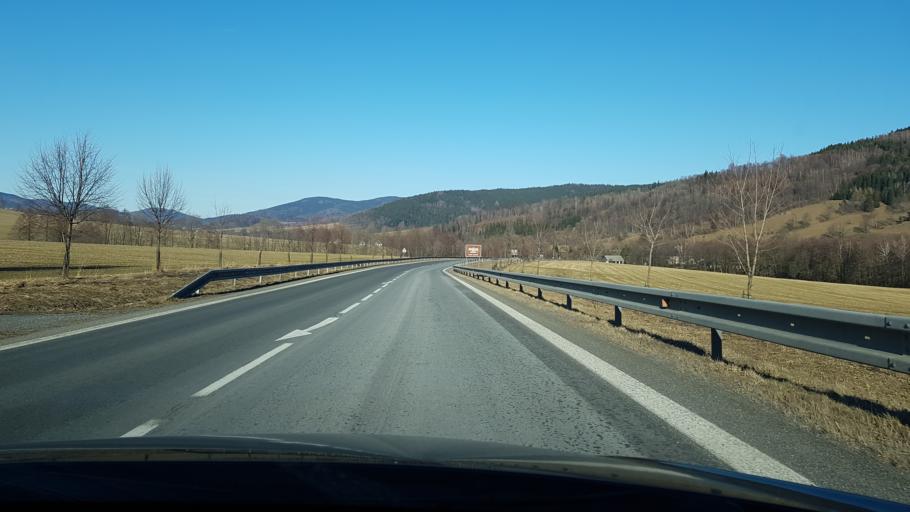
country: CZ
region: Olomoucky
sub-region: Okres Jesenik
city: Jesenik
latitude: 50.1560
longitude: 17.1874
